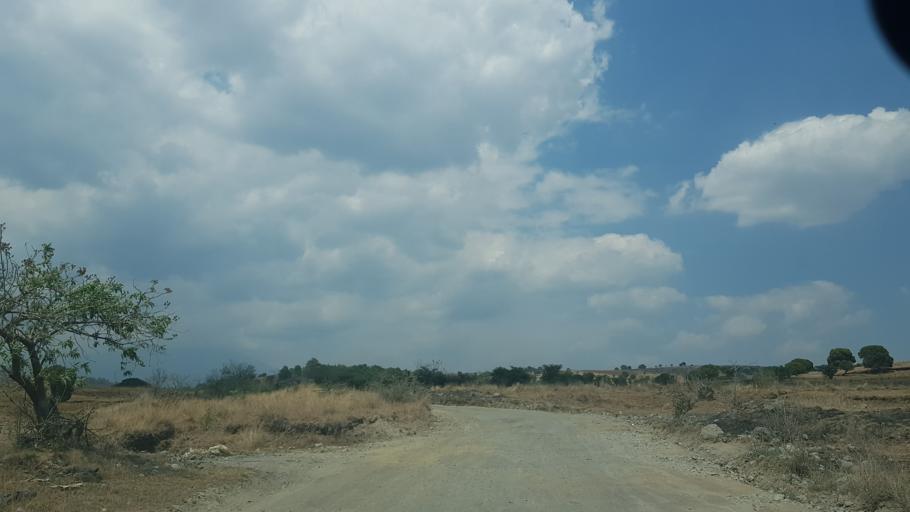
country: MX
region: Puebla
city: San Juan Amecac
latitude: 18.8280
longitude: -98.6224
